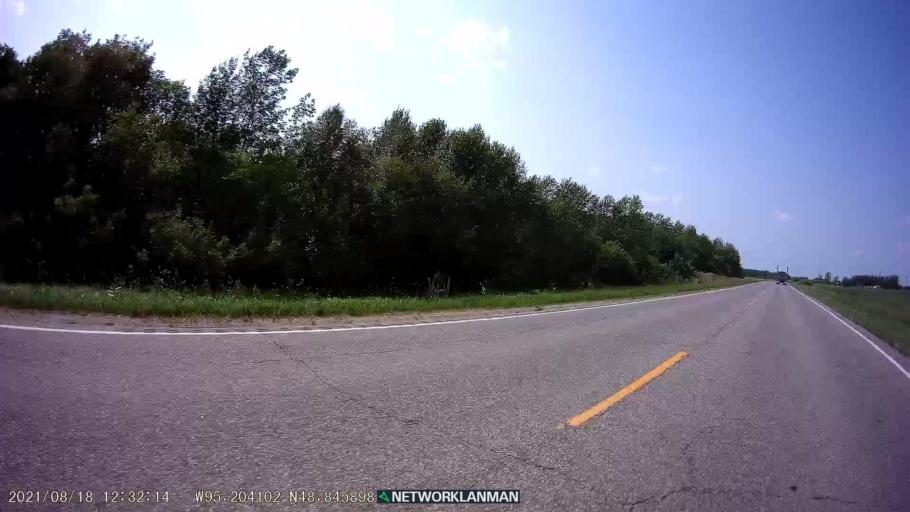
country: US
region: Minnesota
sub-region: Roseau County
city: Warroad
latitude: 48.8462
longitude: -95.2051
